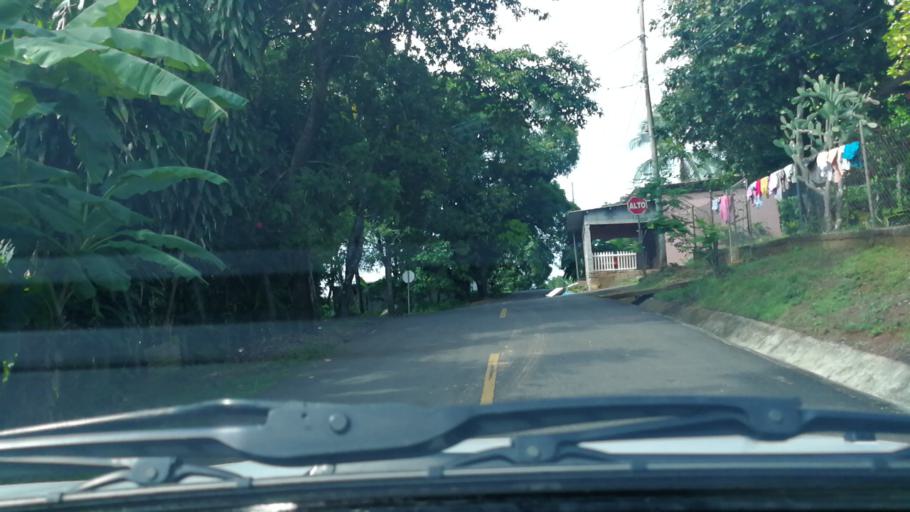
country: PA
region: Panama
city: Pacora
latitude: 9.0833
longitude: -79.2944
